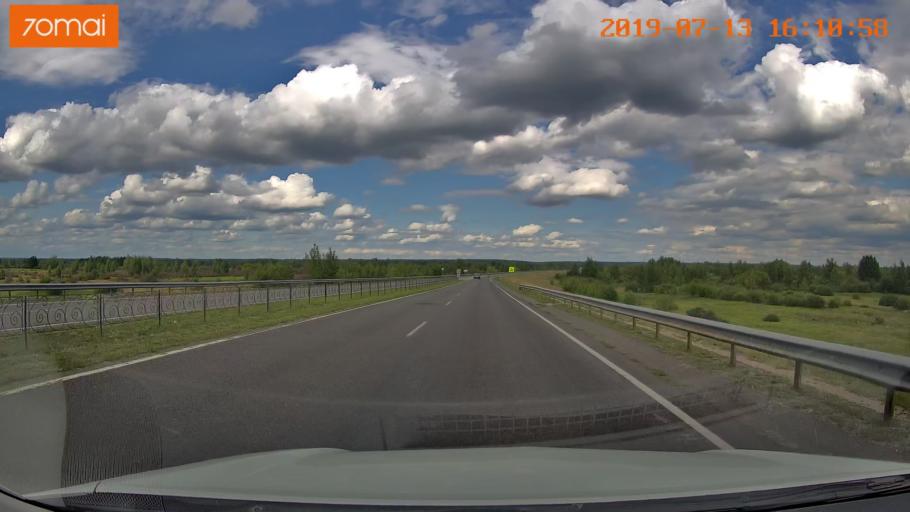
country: BY
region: Mogilev
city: Babruysk
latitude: 53.1640
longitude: 29.2474
